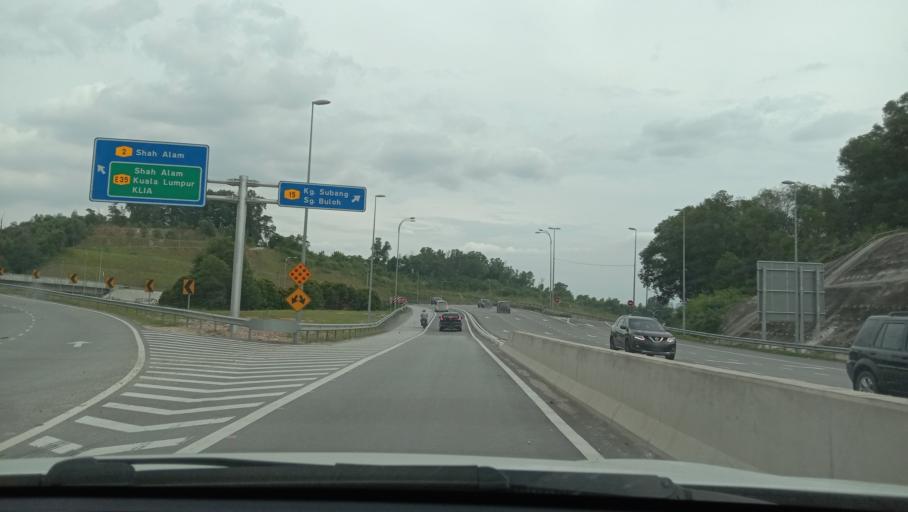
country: MY
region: Selangor
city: Kampung Baru Subang
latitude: 3.1266
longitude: 101.5246
